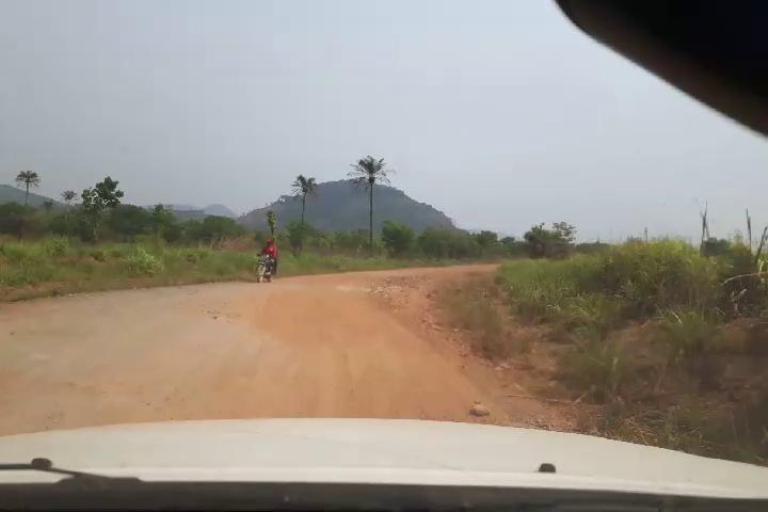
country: SL
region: Northern Province
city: Bumbuna
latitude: 8.8914
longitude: -11.8181
